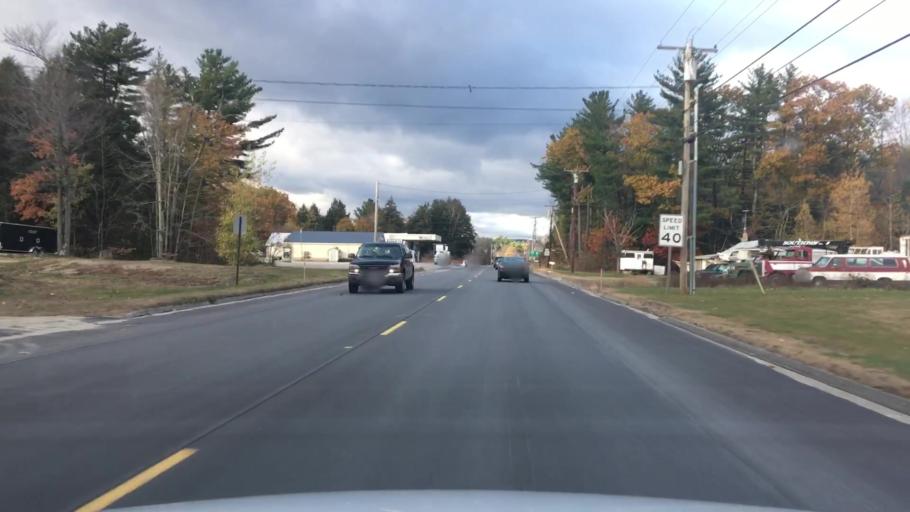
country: US
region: Maine
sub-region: Androscoggin County
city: Livermore
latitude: 44.3744
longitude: -70.2503
